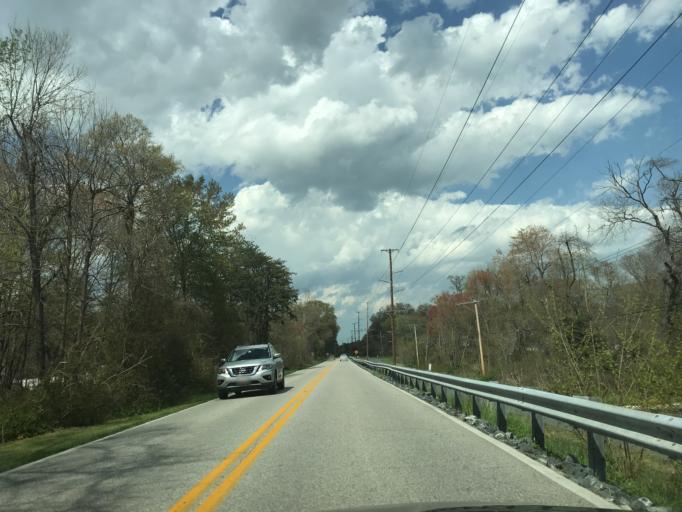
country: US
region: Maryland
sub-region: Anne Arundel County
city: Severn
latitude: 39.1258
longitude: -76.6768
